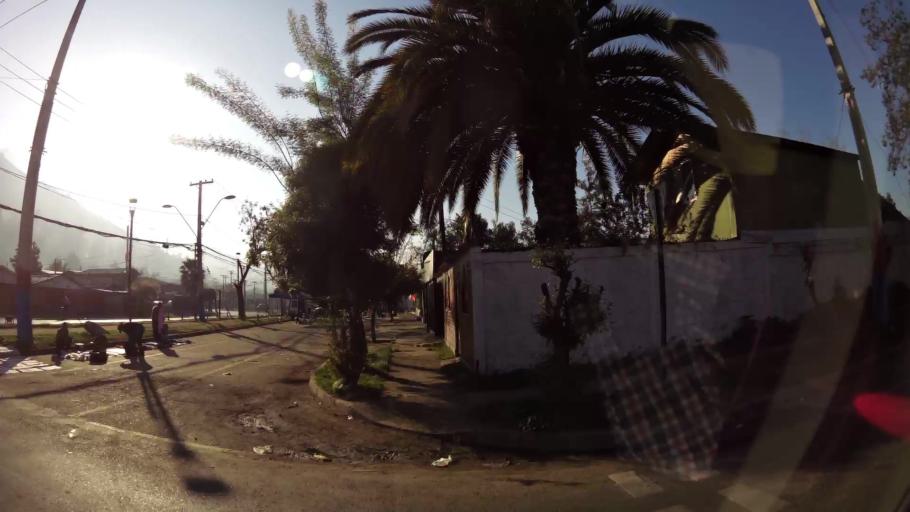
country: CL
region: Santiago Metropolitan
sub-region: Provincia de Santiago
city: Santiago
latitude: -33.3774
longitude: -70.6272
